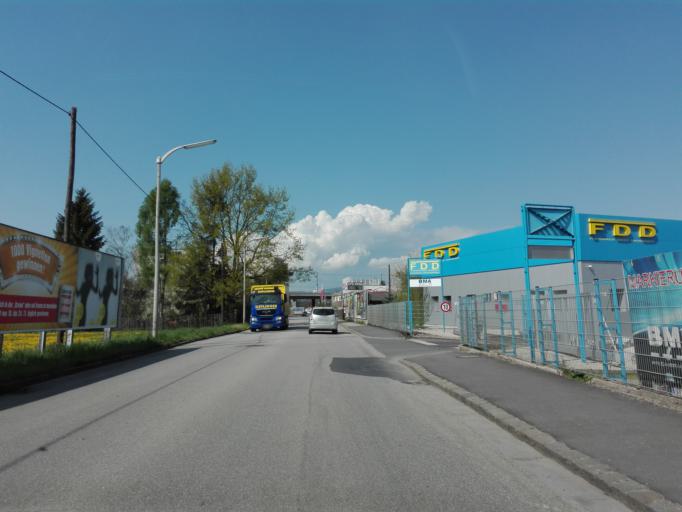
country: AT
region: Upper Austria
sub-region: Politischer Bezirk Linz-Land
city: Leonding
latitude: 48.2500
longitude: 14.2768
